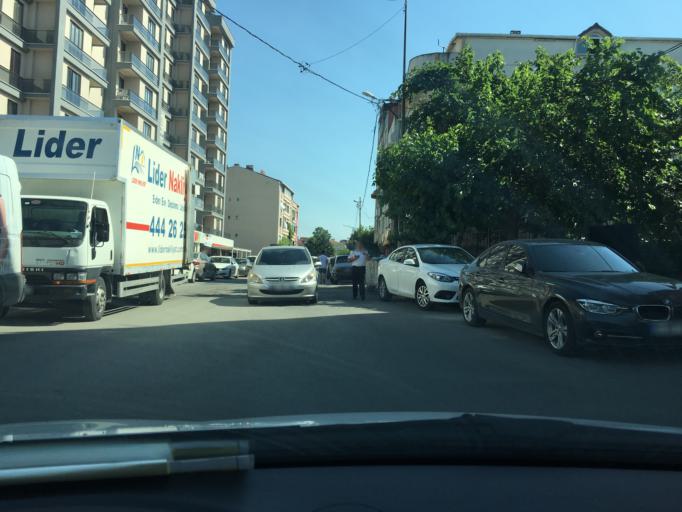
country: TR
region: Istanbul
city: Sisli
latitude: 41.0814
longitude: 28.9440
